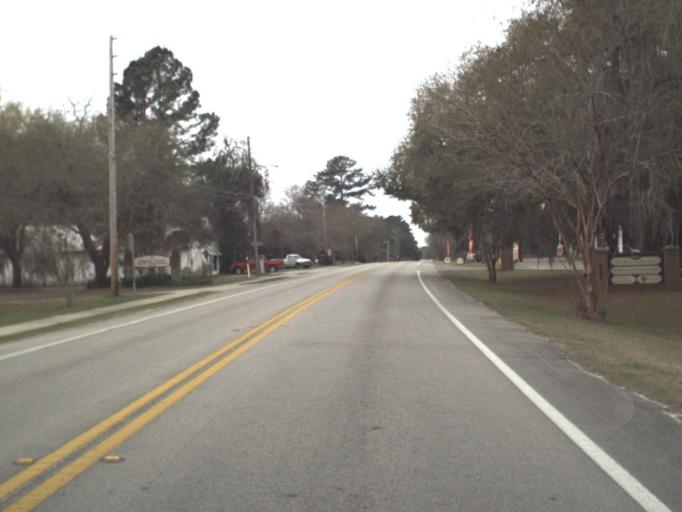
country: US
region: Florida
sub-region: Jefferson County
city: Monticello
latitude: 30.5450
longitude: -83.8802
